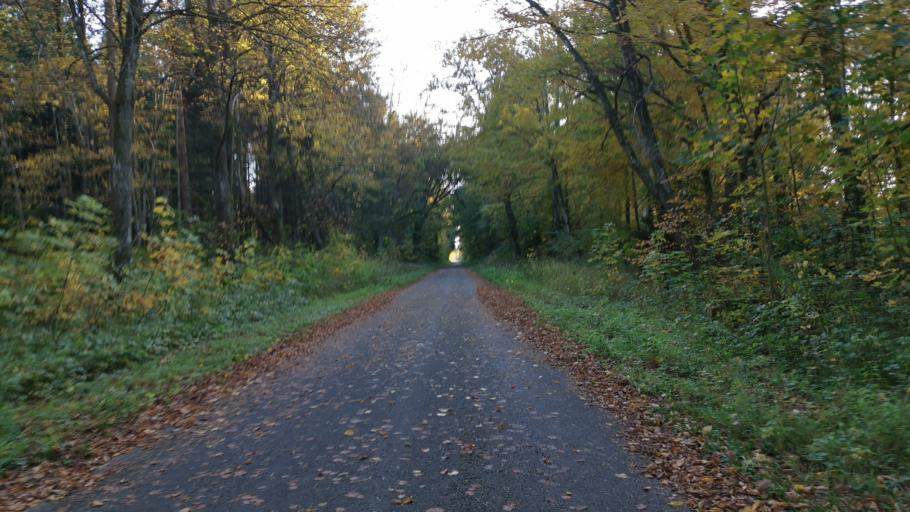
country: DE
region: Bavaria
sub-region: Upper Bavaria
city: Pullach im Isartal
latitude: 48.0618
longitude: 11.5604
